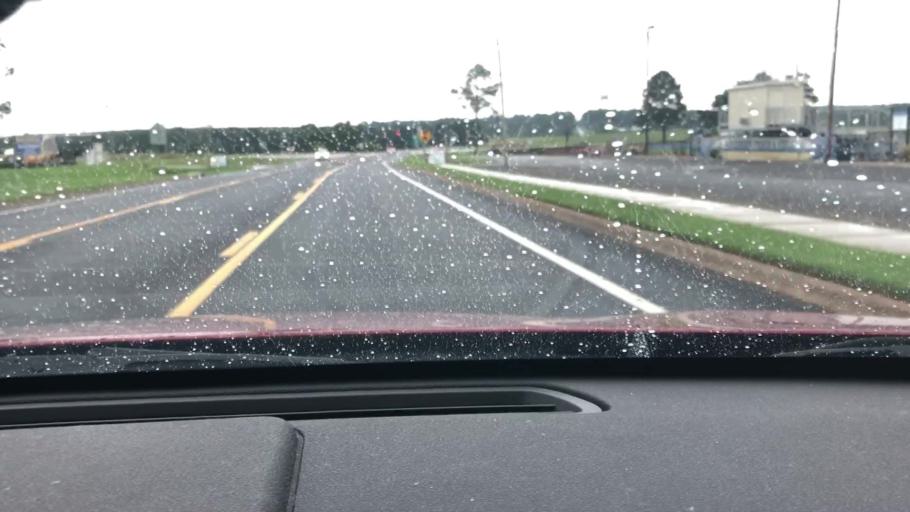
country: US
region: Arkansas
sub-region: Columbia County
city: Magnolia
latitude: 33.2950
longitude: -93.2361
